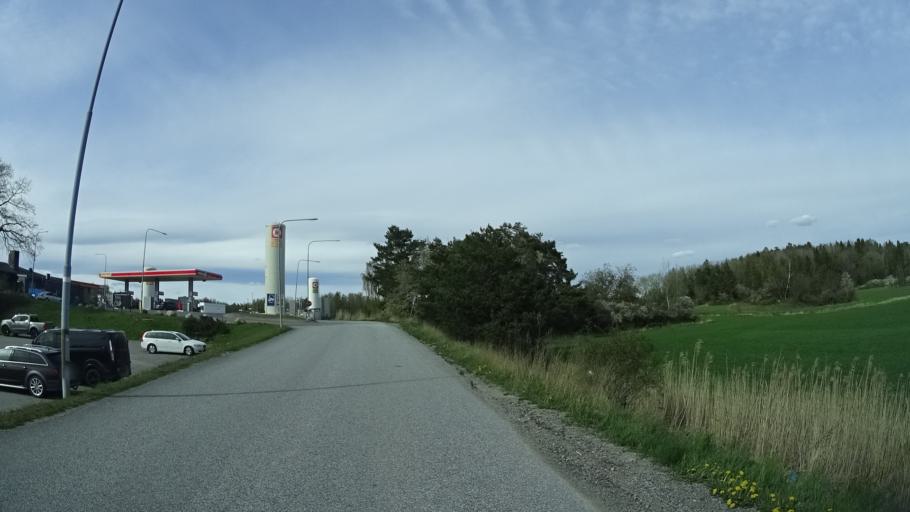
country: SE
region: Stockholm
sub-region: Sodertalje Kommun
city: Pershagen
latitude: 59.0868
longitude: 17.6037
